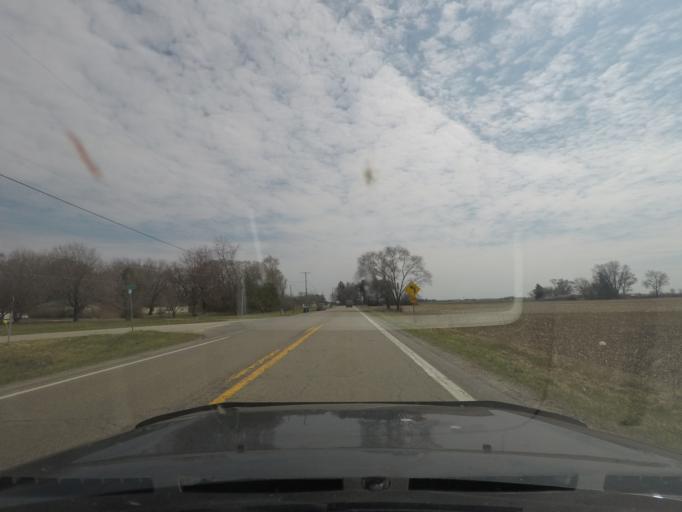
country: US
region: Indiana
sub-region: LaPorte County
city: Kingsford Heights
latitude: 41.4794
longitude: -86.6790
